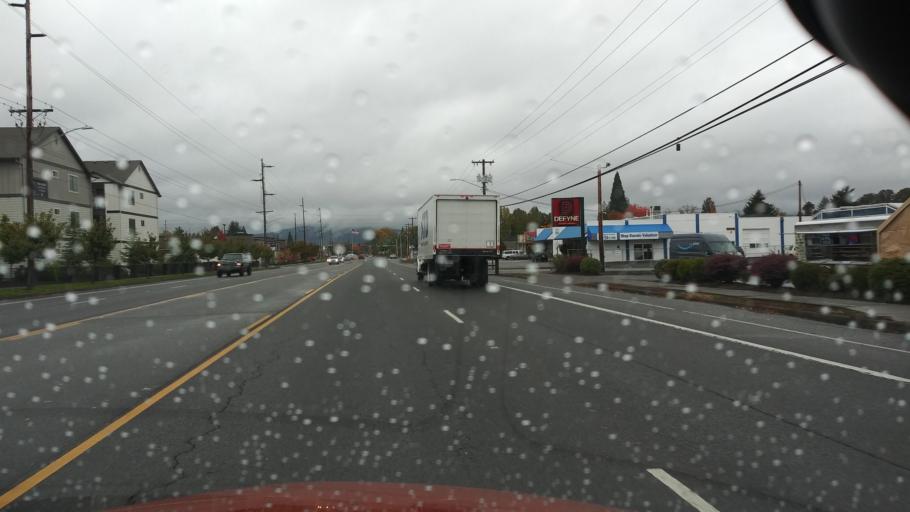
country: US
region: Oregon
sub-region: Washington County
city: Cornelius
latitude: 45.5203
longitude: -123.0798
